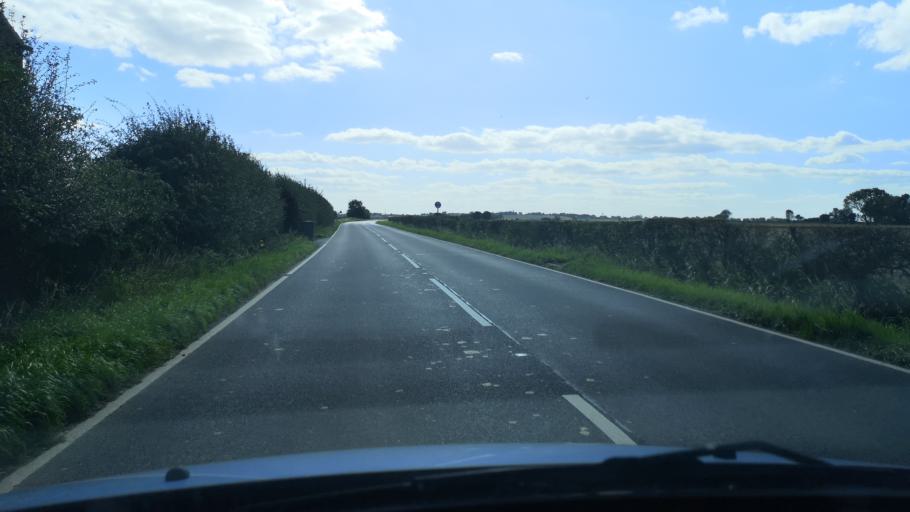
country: GB
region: England
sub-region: North Lincolnshire
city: Eastoft
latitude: 53.6284
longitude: -0.7993
